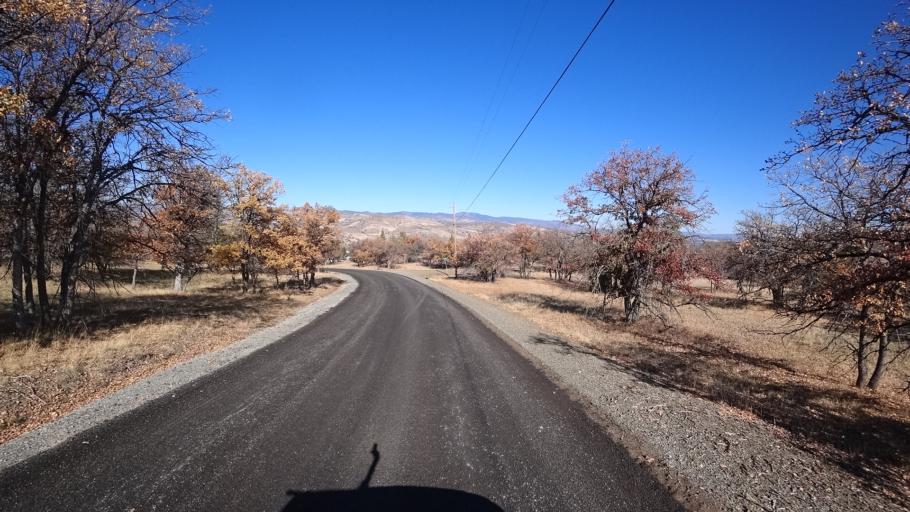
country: US
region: California
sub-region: Siskiyou County
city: Montague
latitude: 41.8801
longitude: -122.4888
